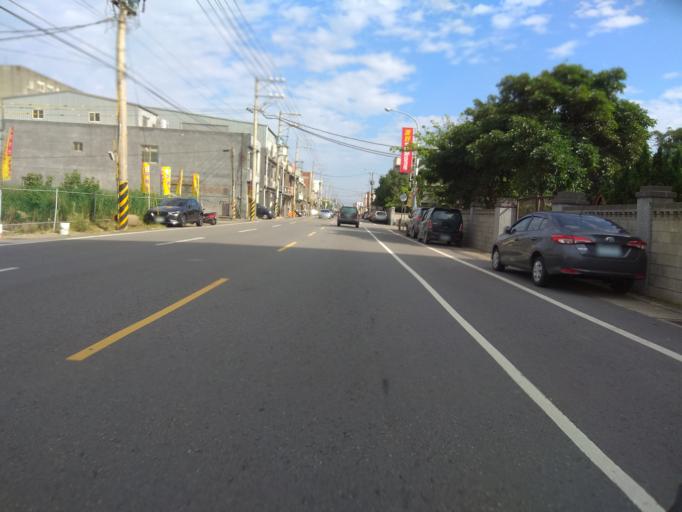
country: TW
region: Taiwan
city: Taoyuan City
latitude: 25.0657
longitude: 121.1870
